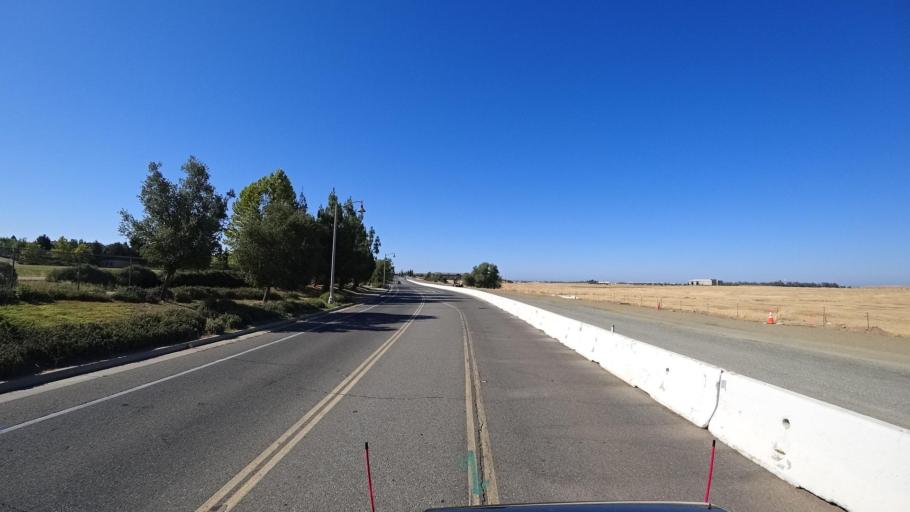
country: US
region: California
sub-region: Placer County
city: Lincoln
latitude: 38.8439
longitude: -121.2906
